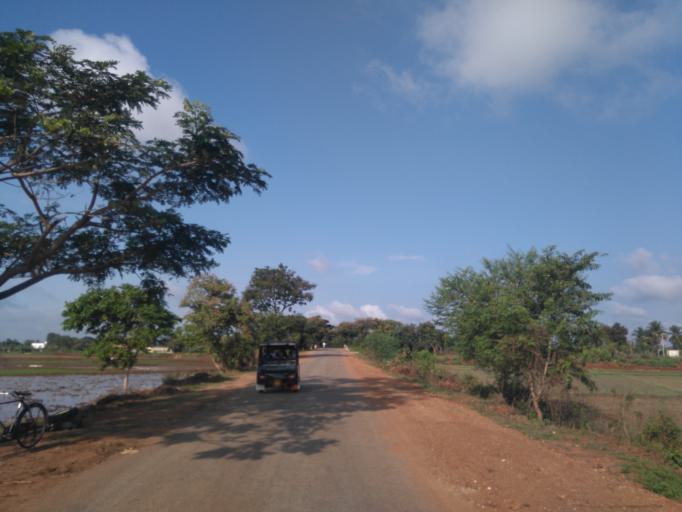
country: IN
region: Karnataka
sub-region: Mandya
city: Malavalli
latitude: 12.2648
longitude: 77.0199
